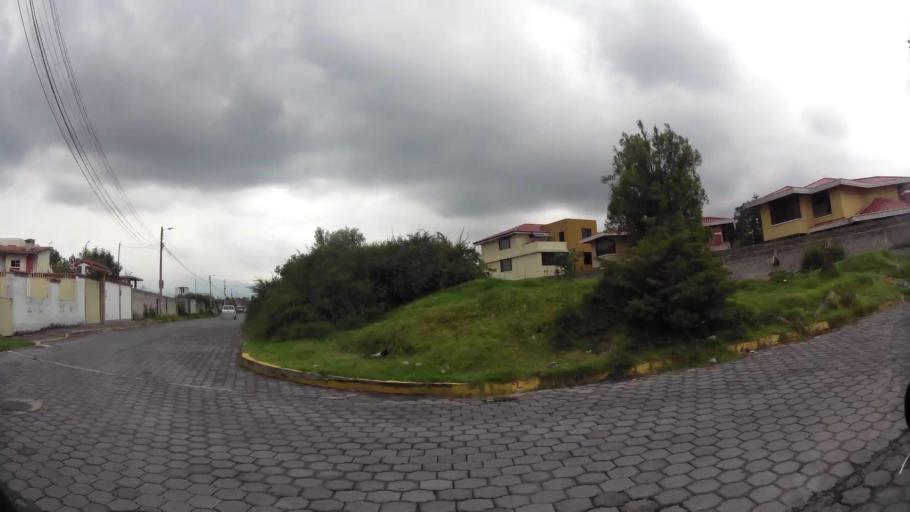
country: EC
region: Pichincha
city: Sangolqui
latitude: -0.3204
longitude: -78.4676
